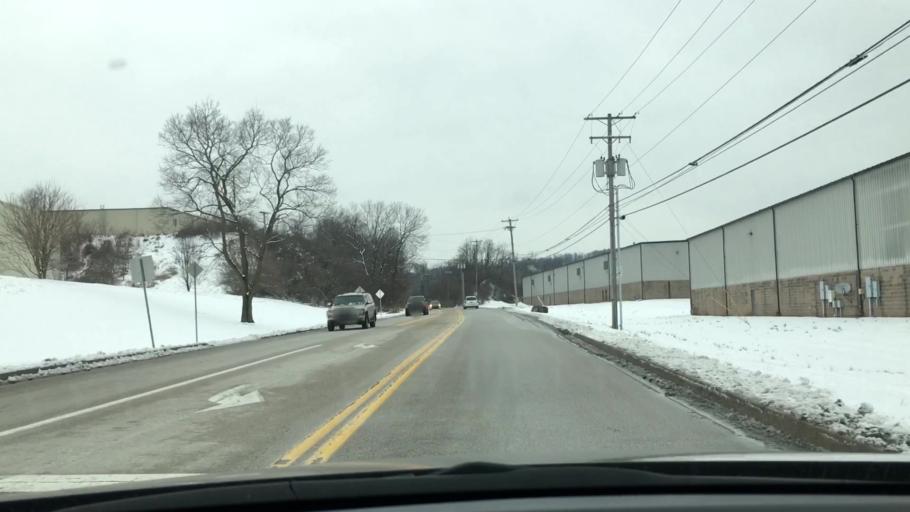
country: US
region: Pennsylvania
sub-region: York County
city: Emigsville
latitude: 40.0129
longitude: -76.7169
